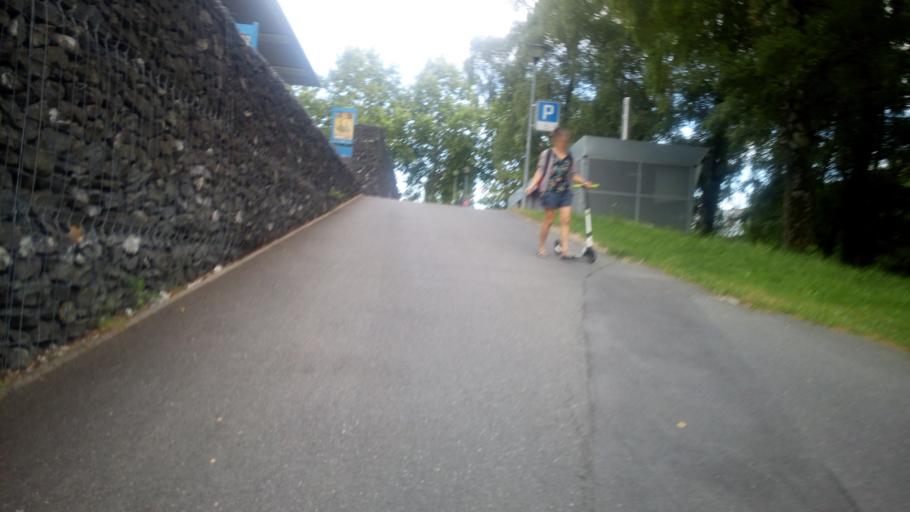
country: CH
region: Vaud
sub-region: Ouest Lausannois District
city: Chavannes
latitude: 46.5217
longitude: 6.5736
